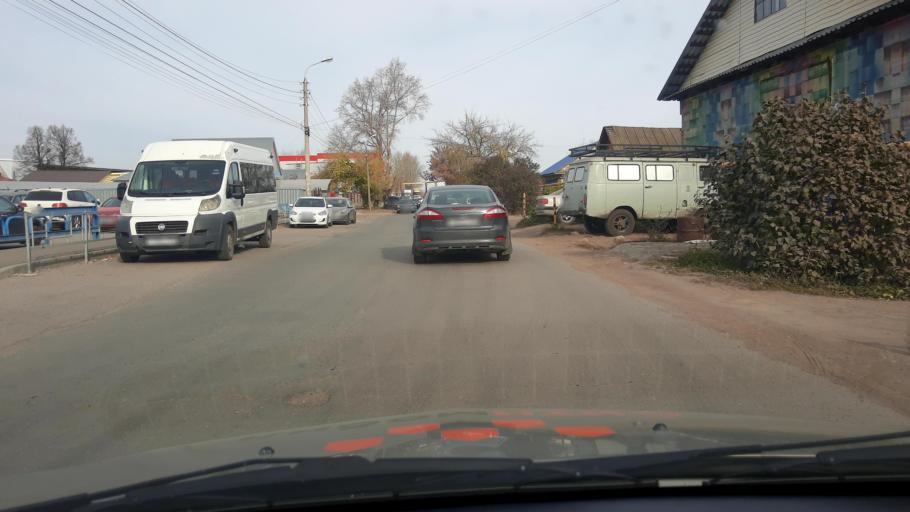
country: RU
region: Bashkortostan
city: Mikhaylovka
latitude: 54.6946
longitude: 55.8493
